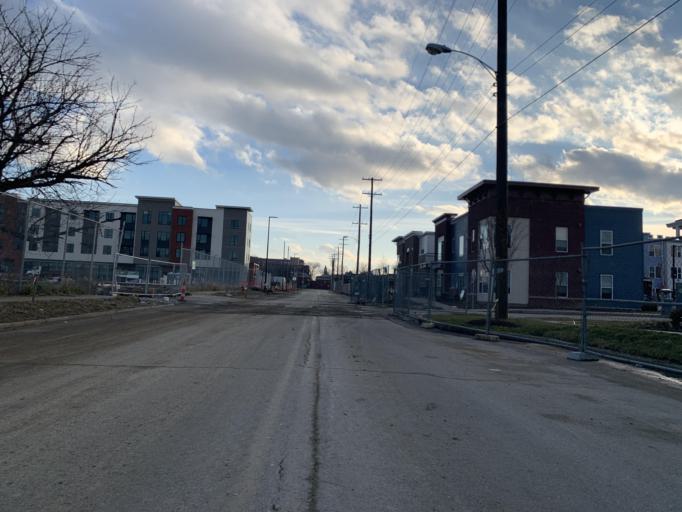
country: US
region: Kentucky
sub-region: Jefferson County
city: Louisville
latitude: 38.2545
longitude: -85.7670
